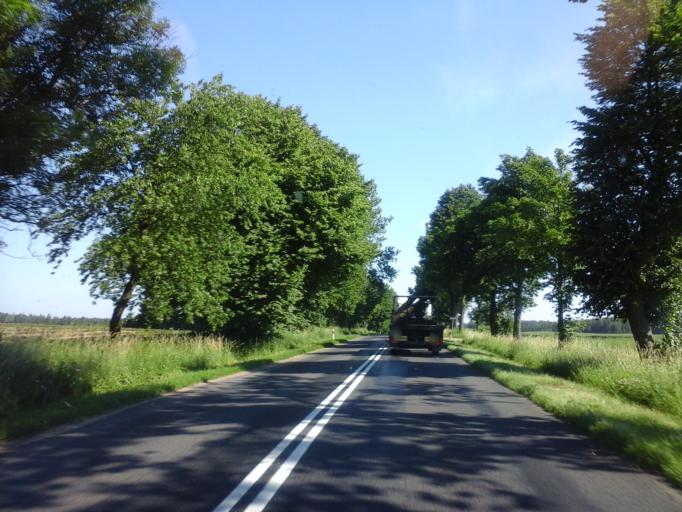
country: PL
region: West Pomeranian Voivodeship
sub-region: Powiat swidwinski
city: Polczyn-Zdroj
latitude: 53.8141
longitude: 16.0753
